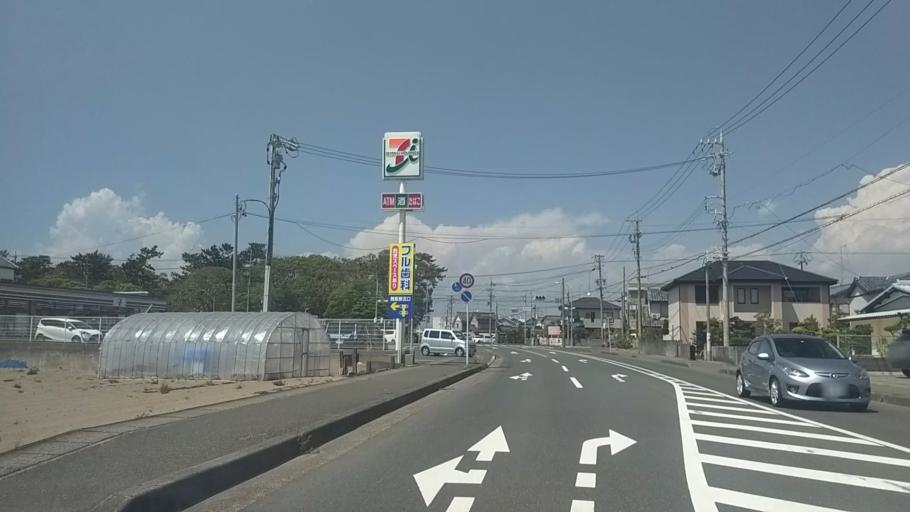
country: JP
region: Shizuoka
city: Hamamatsu
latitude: 34.6826
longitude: 137.6306
